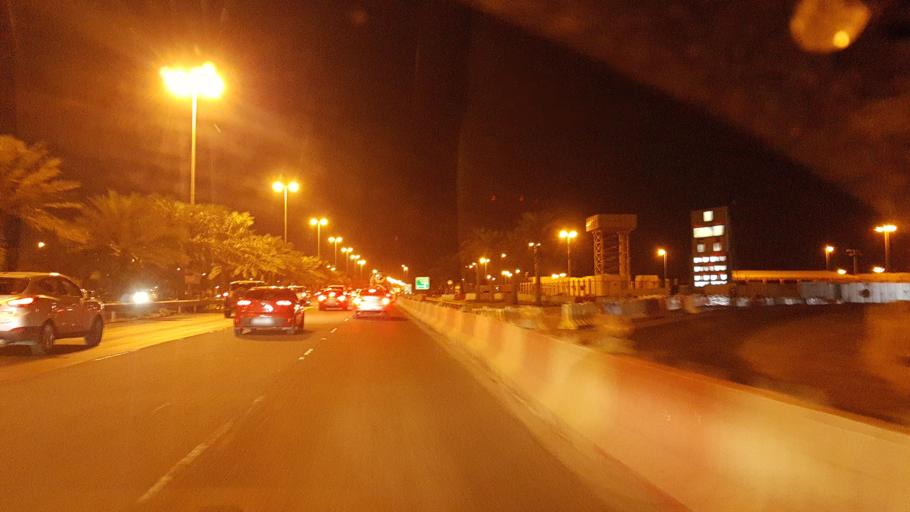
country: BH
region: Muharraq
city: Al Hadd
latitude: 26.2407
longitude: 50.6581
